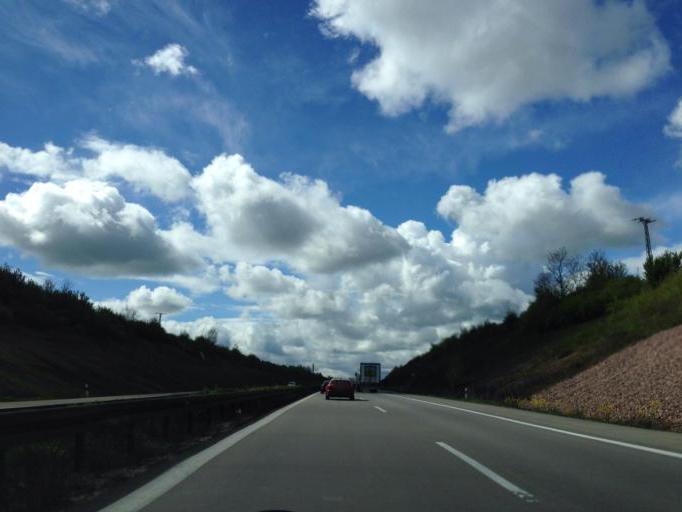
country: DE
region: Saxony-Anhalt
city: Wallwitz
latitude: 51.5693
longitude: 11.9289
